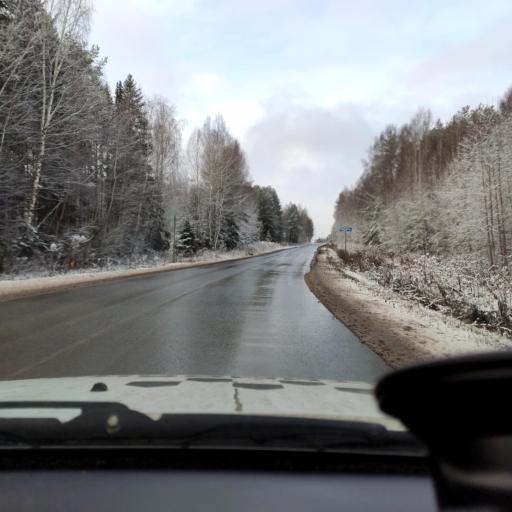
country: RU
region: Perm
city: Nytva
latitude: 57.9284
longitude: 55.3940
